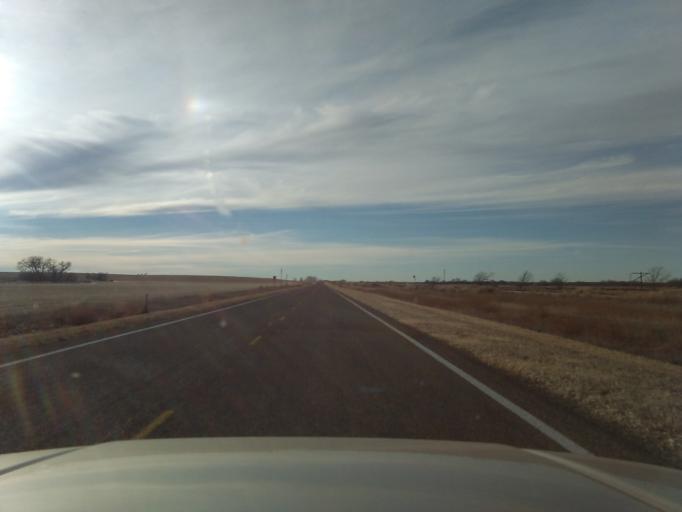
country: US
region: Kansas
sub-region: Norton County
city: Norton
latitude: 39.7539
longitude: -100.1295
